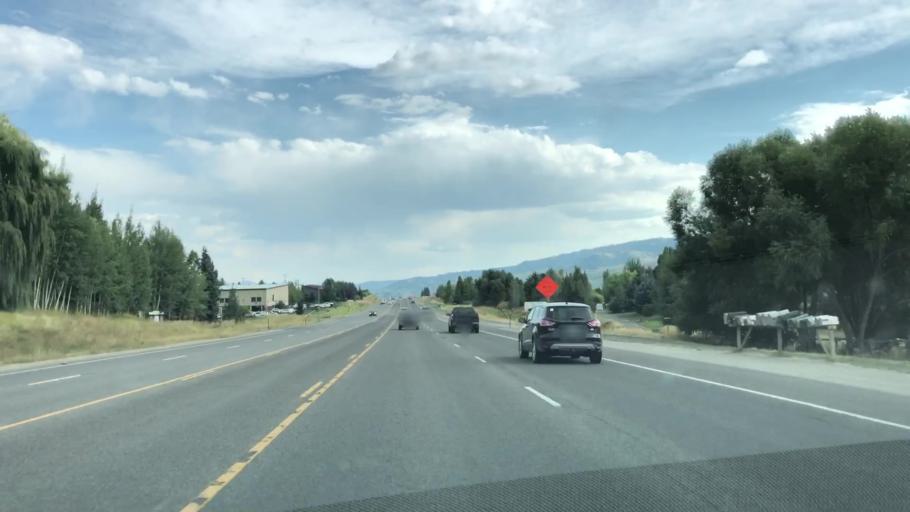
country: US
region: Wyoming
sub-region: Teton County
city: South Park
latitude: 43.4268
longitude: -110.7785
